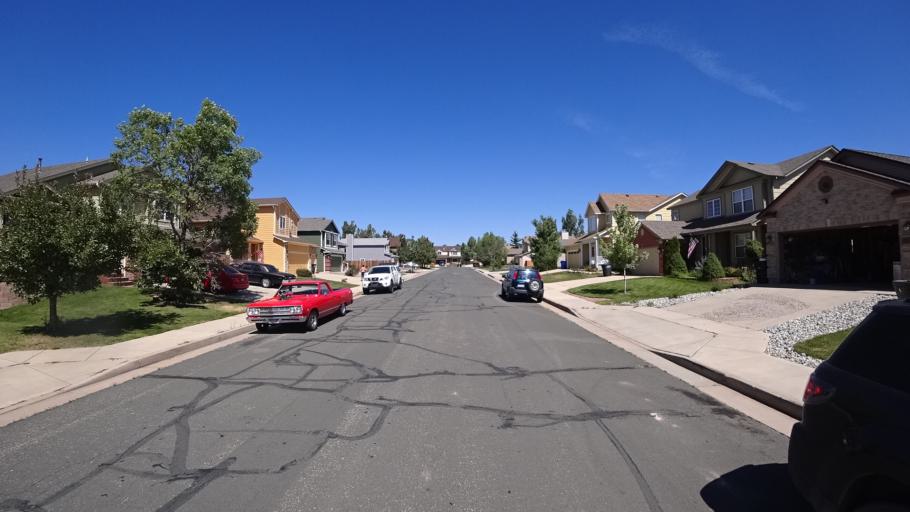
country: US
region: Colorado
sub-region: El Paso County
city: Black Forest
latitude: 38.9500
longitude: -104.7575
